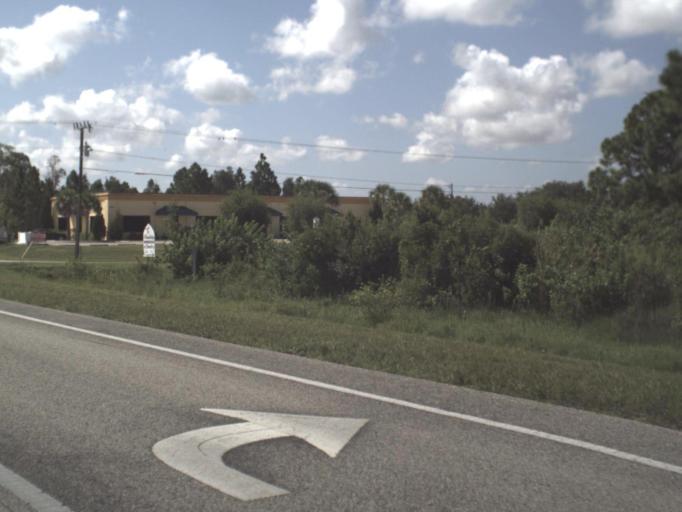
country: US
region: Florida
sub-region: Charlotte County
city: Charlotte Park
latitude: 26.8544
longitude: -81.9856
